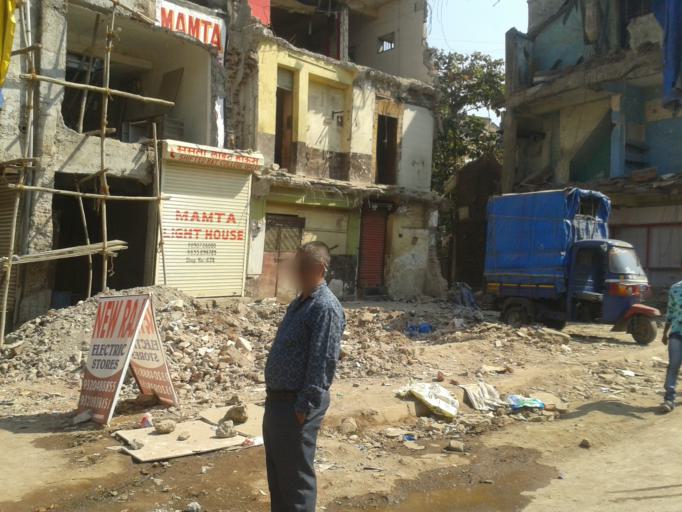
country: IN
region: Maharashtra
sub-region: Thane
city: Ulhasnagar
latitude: 19.2277
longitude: 73.1612
